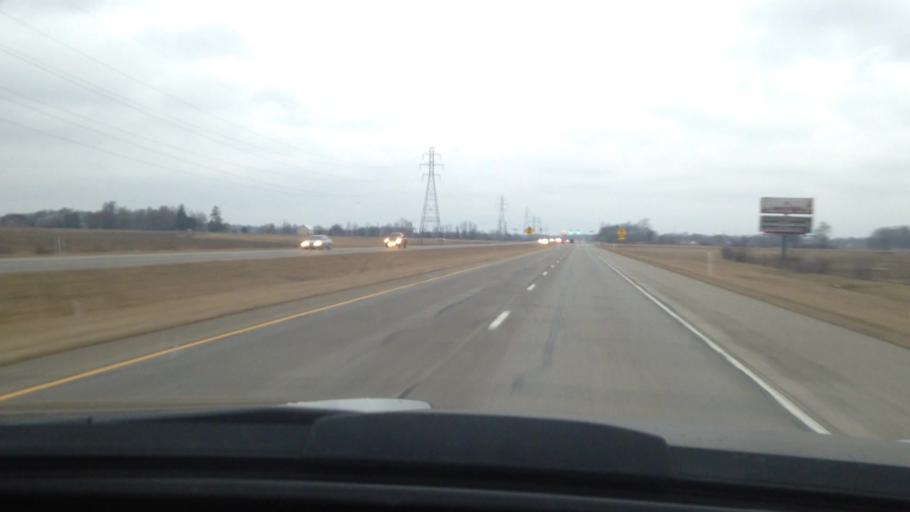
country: US
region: Indiana
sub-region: Delaware County
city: Muncie
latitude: 40.1419
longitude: -85.3978
